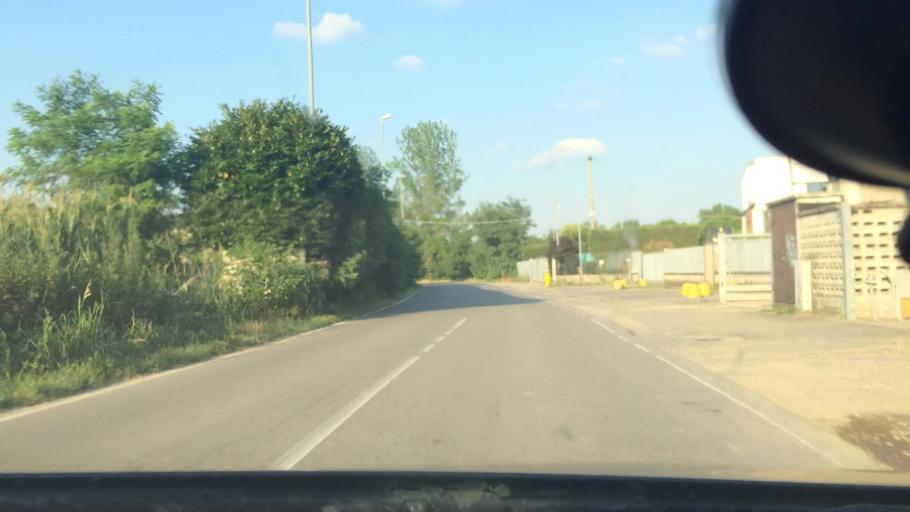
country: IT
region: Lombardy
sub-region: Citta metropolitana di Milano
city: Mantegazza
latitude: 45.5081
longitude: 8.9643
